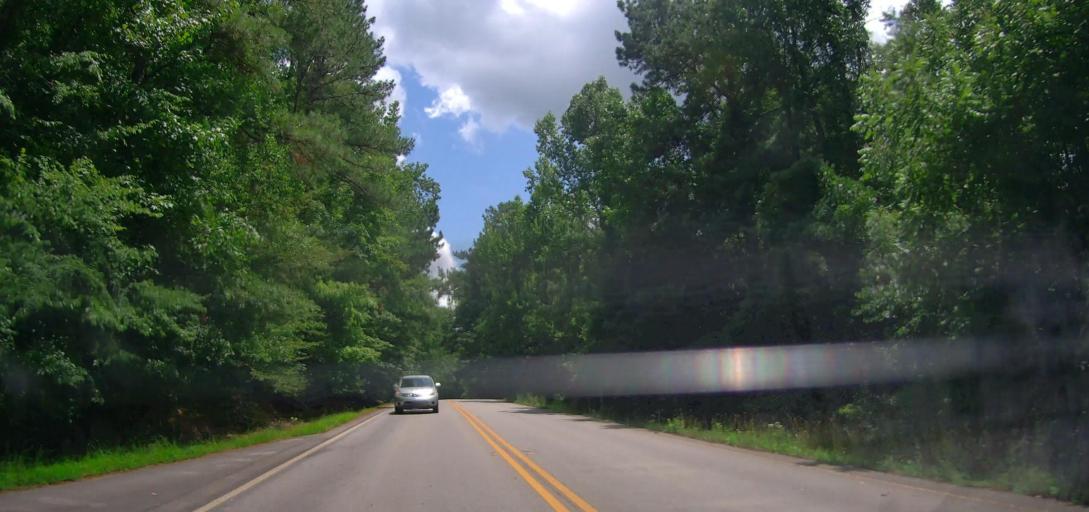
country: US
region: Georgia
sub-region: Troup County
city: Hogansville
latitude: 33.1425
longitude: -84.8415
